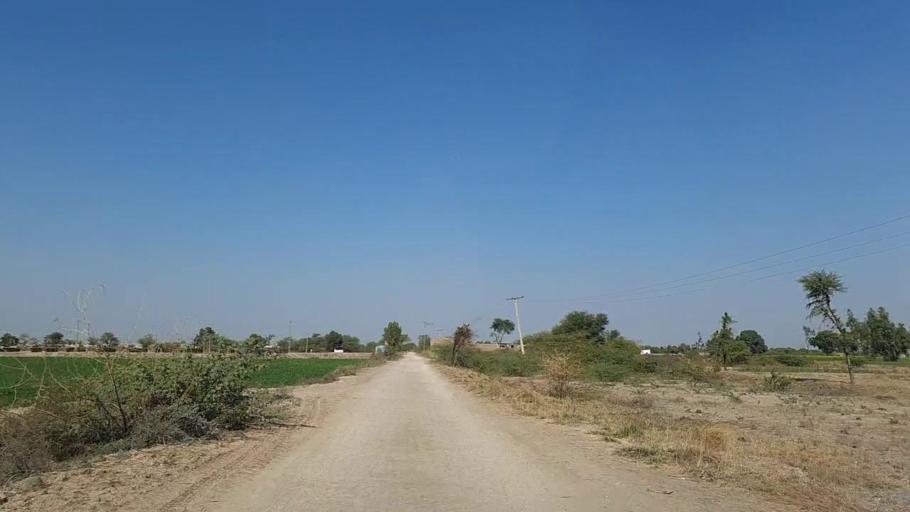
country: PK
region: Sindh
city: Nawabshah
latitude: 26.2521
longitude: 68.4411
